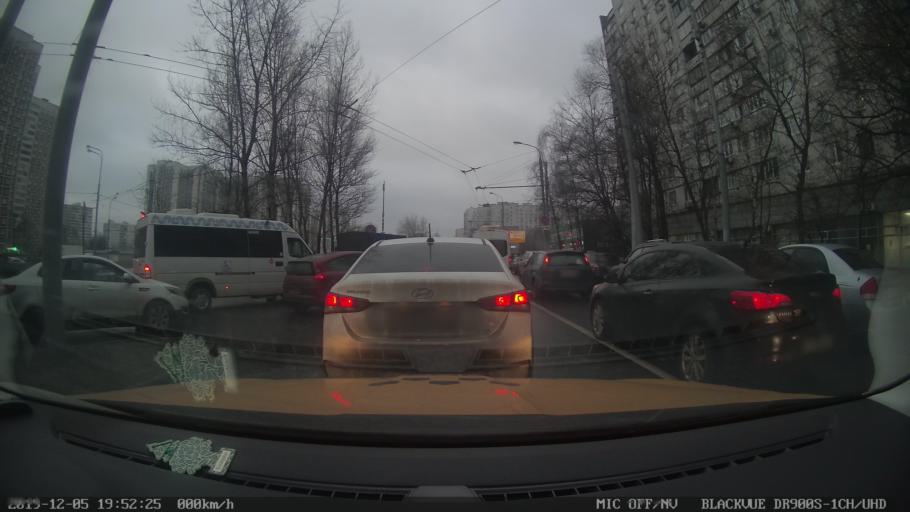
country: RU
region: Moscow
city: Lianozovo
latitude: 55.8999
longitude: 37.5863
